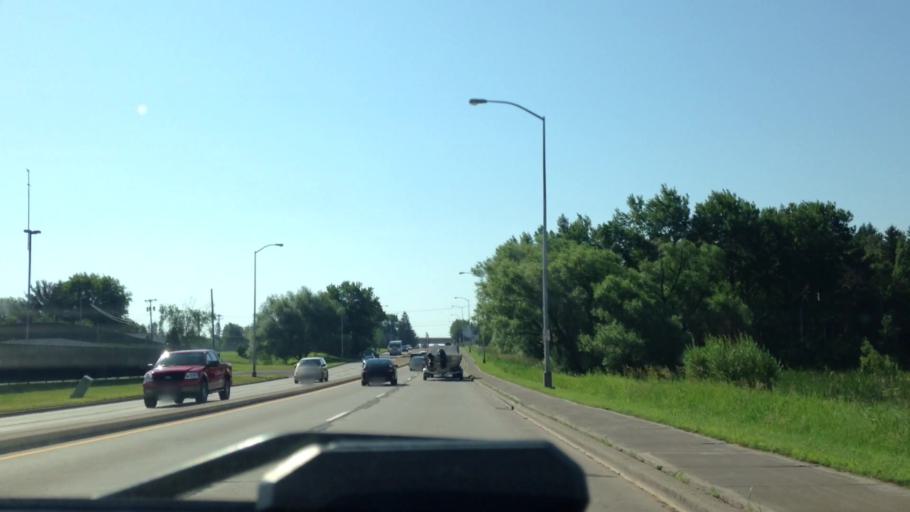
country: US
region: Wisconsin
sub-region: Douglas County
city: Superior
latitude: 46.6938
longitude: -92.0311
